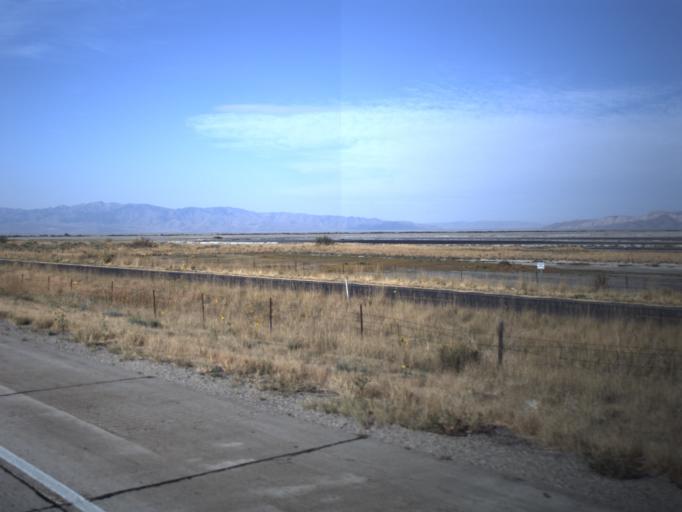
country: US
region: Utah
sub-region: Salt Lake County
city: Magna
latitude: 40.7668
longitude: -112.1570
